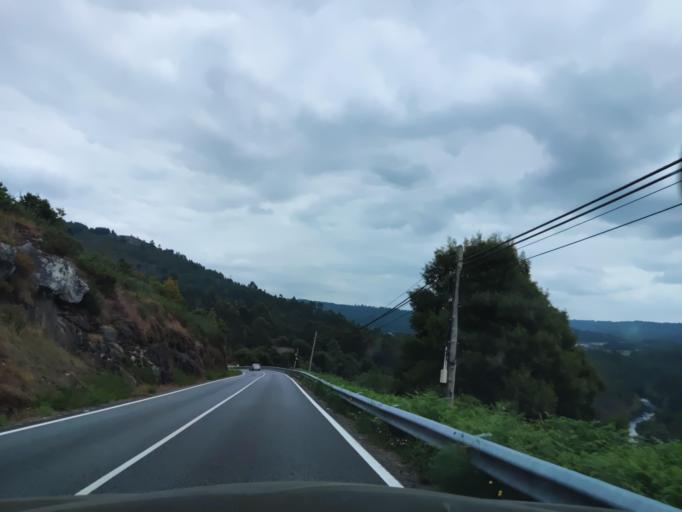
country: ES
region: Galicia
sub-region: Provincia da Coruna
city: Padron
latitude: 42.7434
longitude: -8.6232
